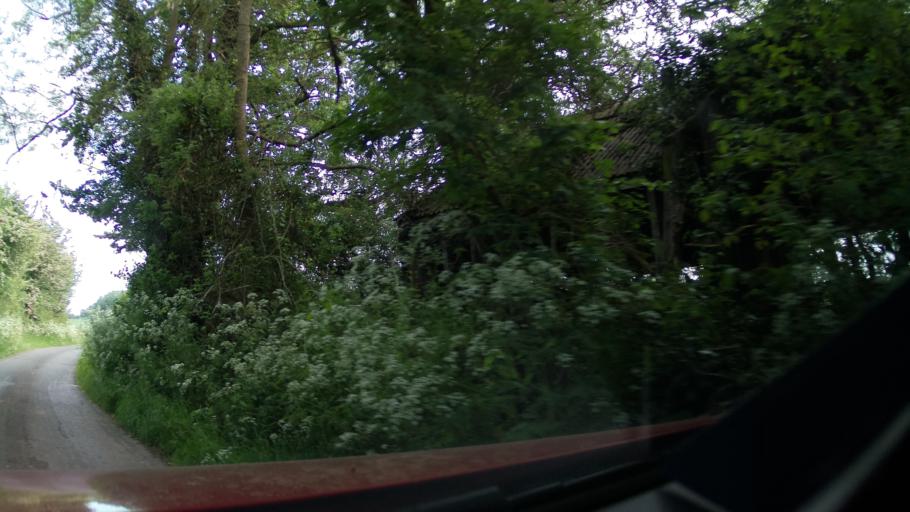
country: GB
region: England
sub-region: Gloucestershire
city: Moreton in Marsh
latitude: 52.0306
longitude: -1.7190
